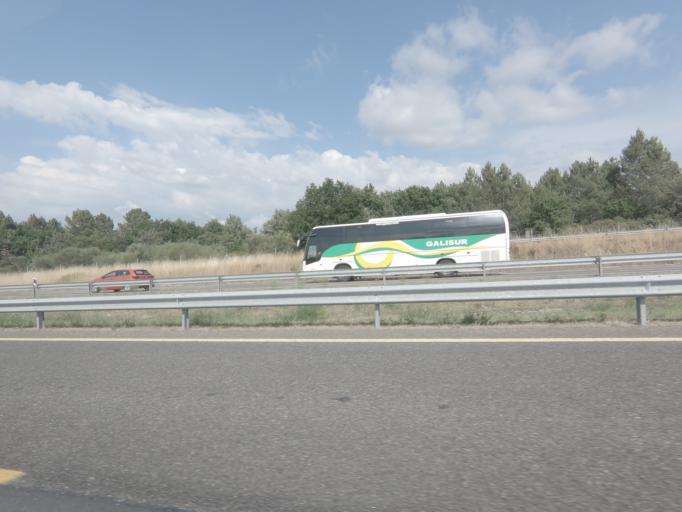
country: ES
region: Galicia
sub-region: Provincia de Ourense
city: Taboadela
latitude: 42.2577
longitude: -7.8689
